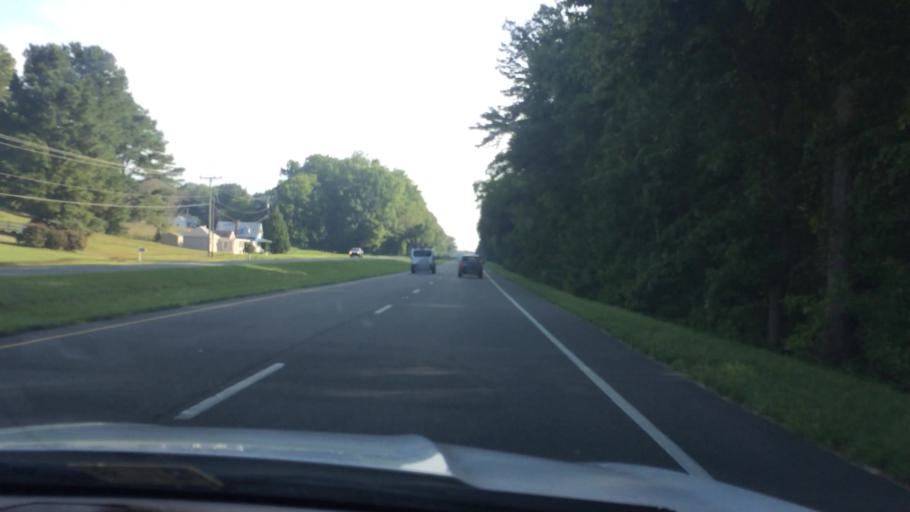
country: US
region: Virginia
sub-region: Gloucester County
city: Gloucester Courthouse
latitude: 37.4282
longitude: -76.4827
